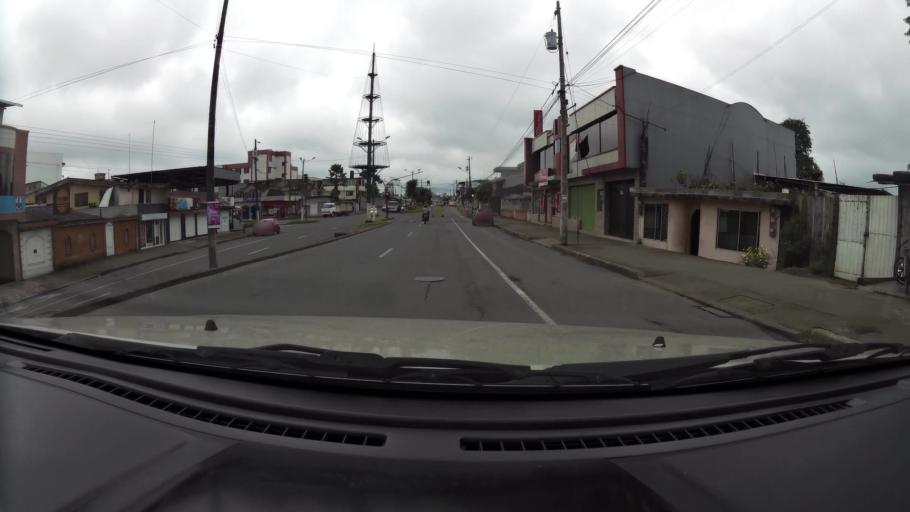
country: EC
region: Santo Domingo de los Tsachilas
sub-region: Canton Santo Domingo de los Colorados
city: Santo Domingo de los Colorados
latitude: -0.2588
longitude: -79.1611
